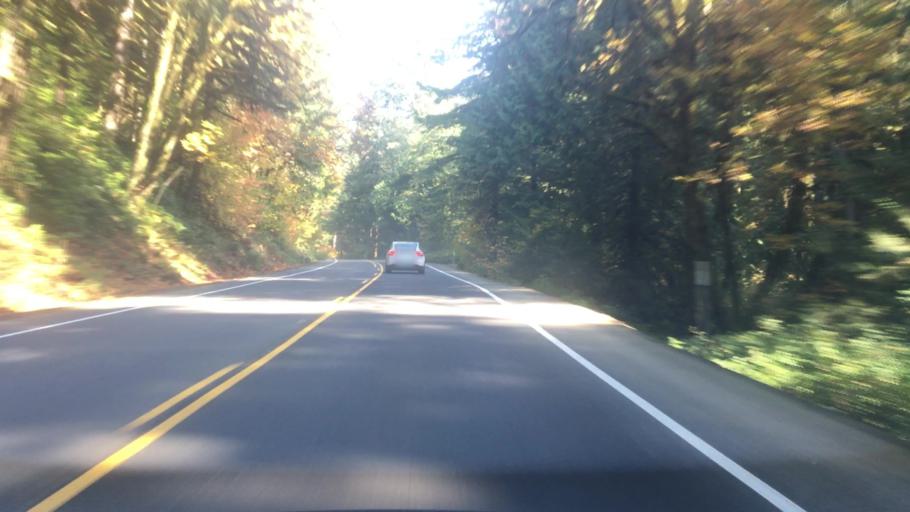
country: US
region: Oregon
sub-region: Lincoln County
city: Rose Lodge
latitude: 45.0529
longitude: -123.7726
